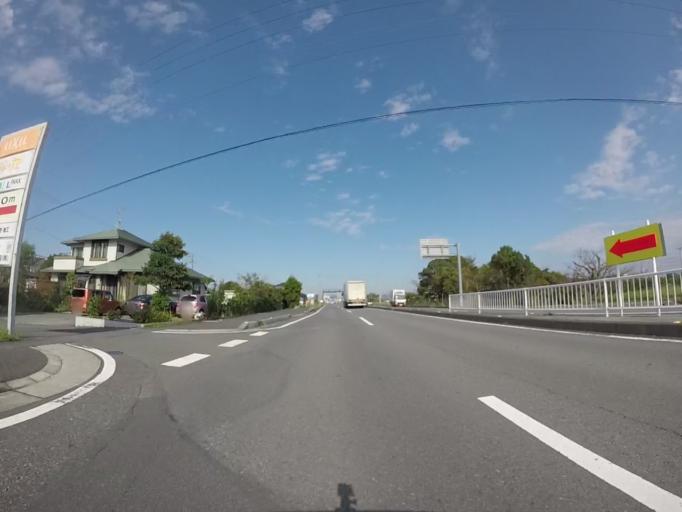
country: JP
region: Shizuoka
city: Shimada
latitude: 34.7876
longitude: 138.2433
